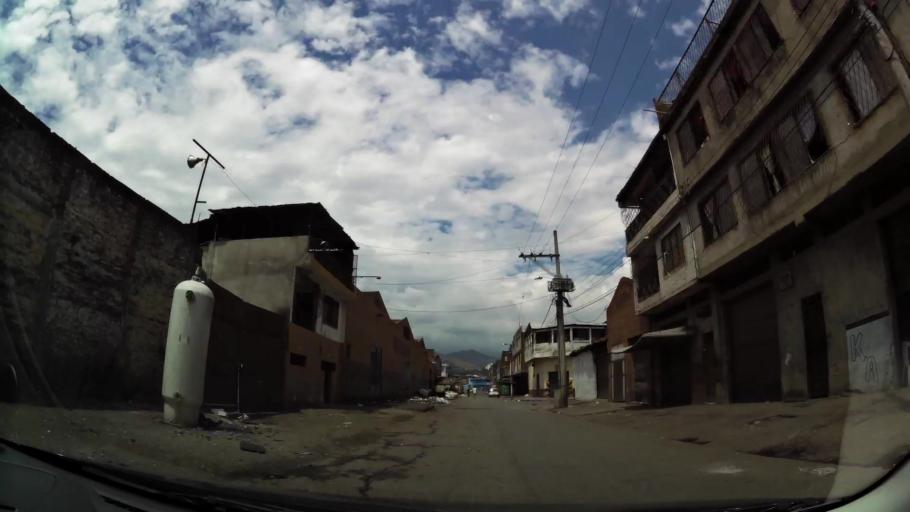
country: CO
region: Valle del Cauca
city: Cali
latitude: 3.4460
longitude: -76.5252
